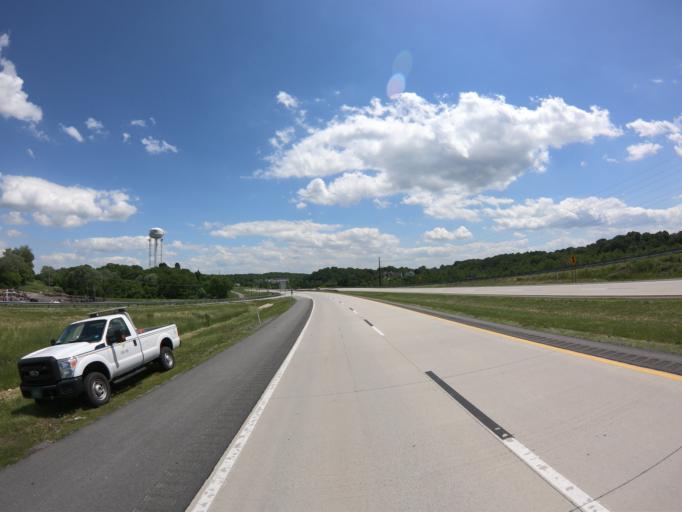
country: US
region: West Virginia
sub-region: Berkeley County
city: Martinsburg
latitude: 39.3987
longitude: -77.9221
